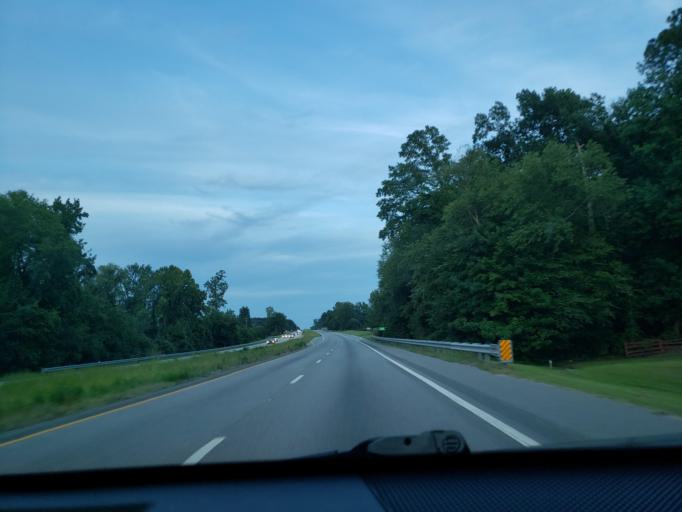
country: US
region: Virginia
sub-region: Southampton County
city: Courtland
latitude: 36.7053
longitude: -77.1929
